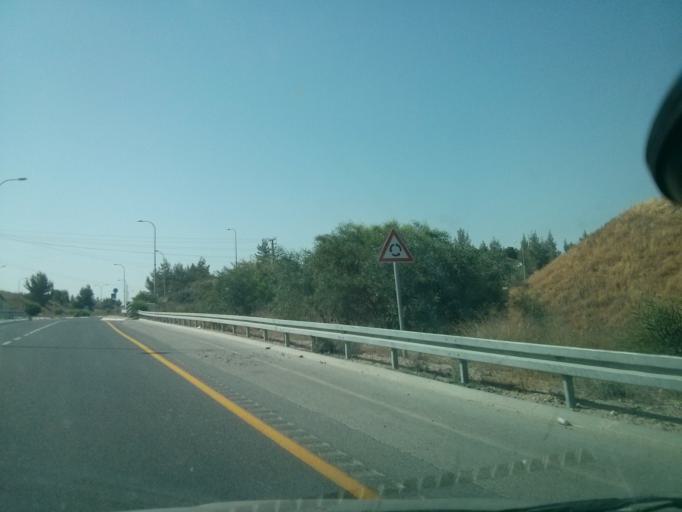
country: IL
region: Jerusalem
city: Bet Shemesh
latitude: 31.7075
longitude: 35.0068
